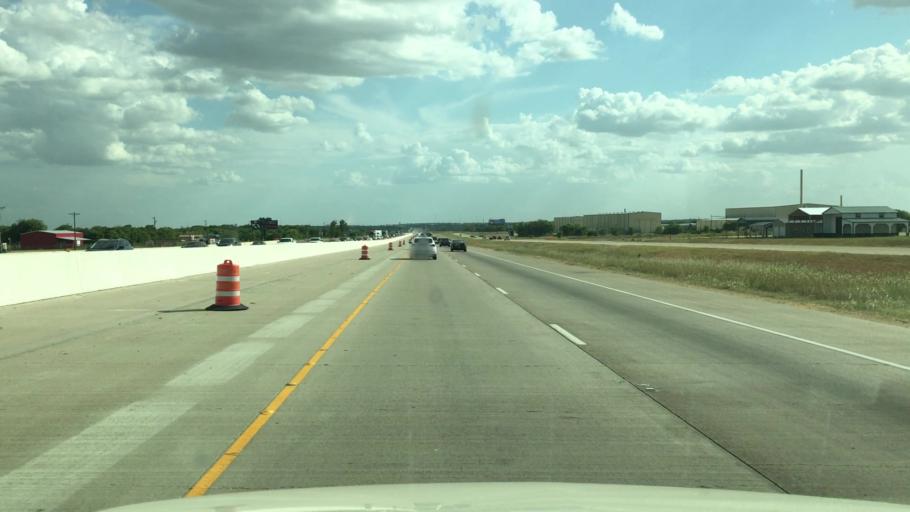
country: US
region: Texas
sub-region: Bell County
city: Troy
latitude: 31.2532
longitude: -97.2772
